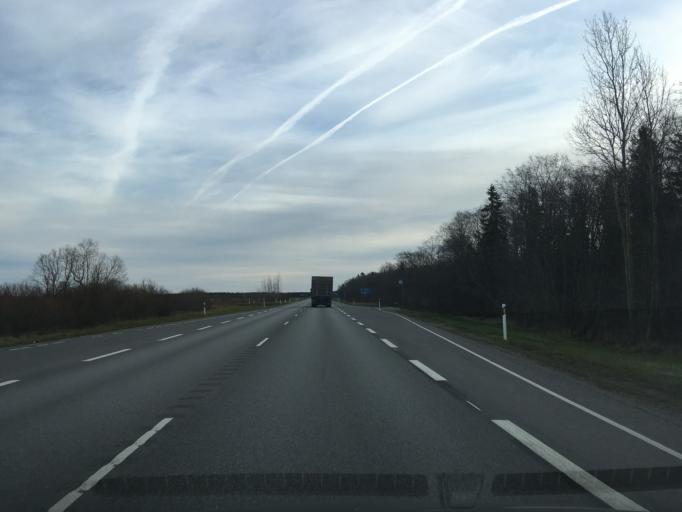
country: EE
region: Ida-Virumaa
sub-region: Kohtla-Jaerve linn
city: Kohtla-Jarve
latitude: 59.4210
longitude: 27.2143
